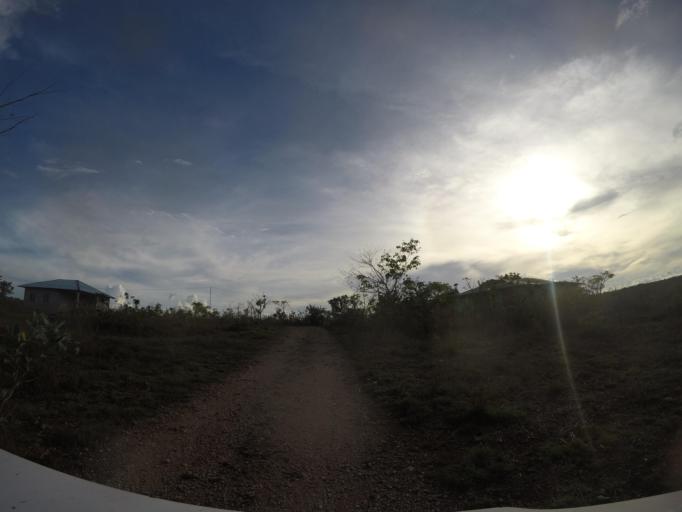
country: TL
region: Baucau
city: Baucau
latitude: -8.4879
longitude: 126.4501
